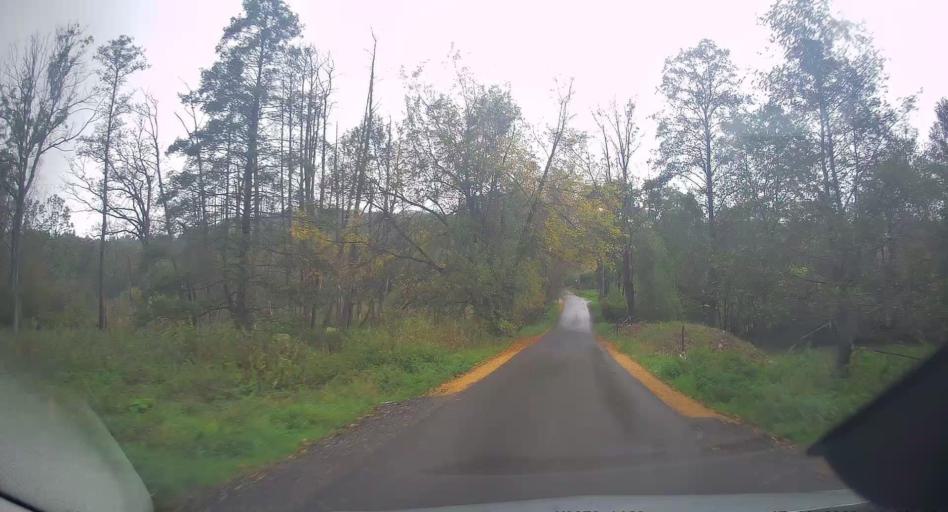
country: PL
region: Lesser Poland Voivodeship
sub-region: Powiat krakowski
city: Ochojno
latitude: 49.9887
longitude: 19.9886
